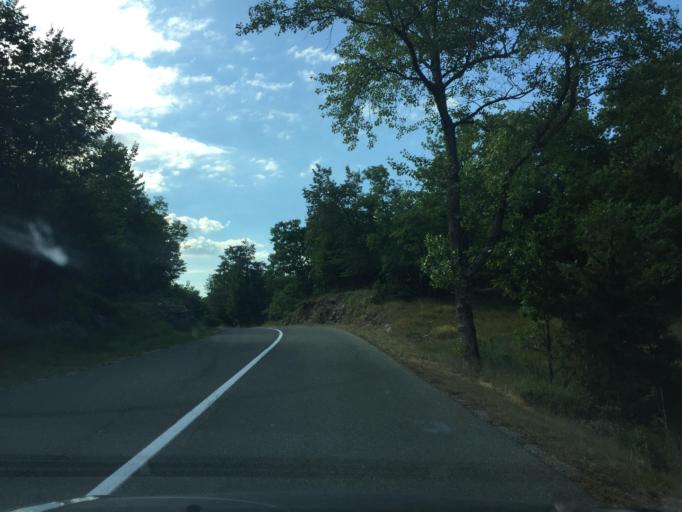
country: HR
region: Primorsko-Goranska
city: Klana
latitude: 45.4463
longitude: 14.3266
